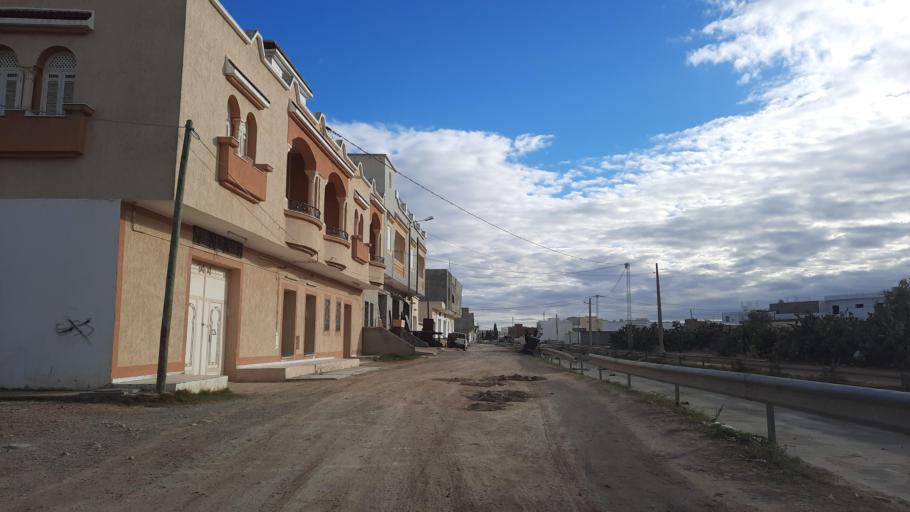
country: TN
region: Al Mahdiyah
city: El Jem
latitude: 35.2900
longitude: 10.7034
